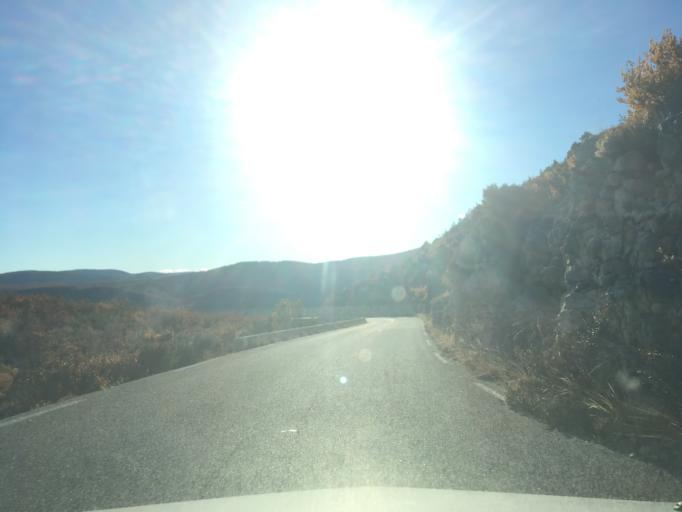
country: FR
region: Provence-Alpes-Cote d'Azur
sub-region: Departement des Alpes-de-Haute-Provence
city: Castellane
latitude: 43.7501
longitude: 6.3987
